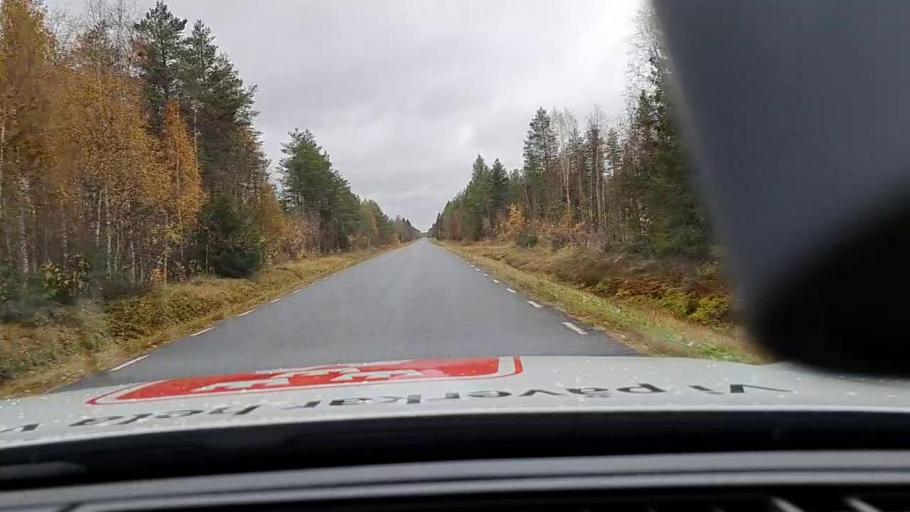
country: SE
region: Norrbotten
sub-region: Haparanda Kommun
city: Haparanda
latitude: 65.9103
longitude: 23.8298
